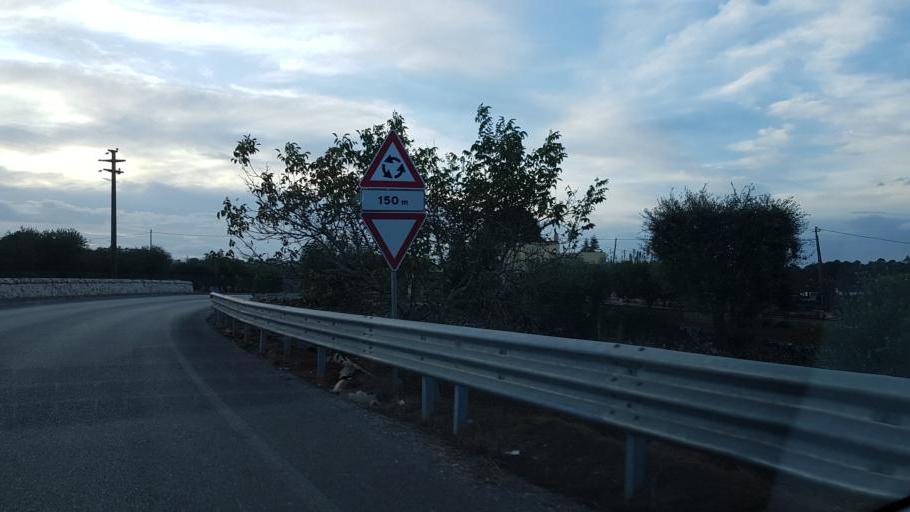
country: IT
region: Apulia
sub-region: Provincia di Bari
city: Locorotondo
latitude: 40.7641
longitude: 17.3302
